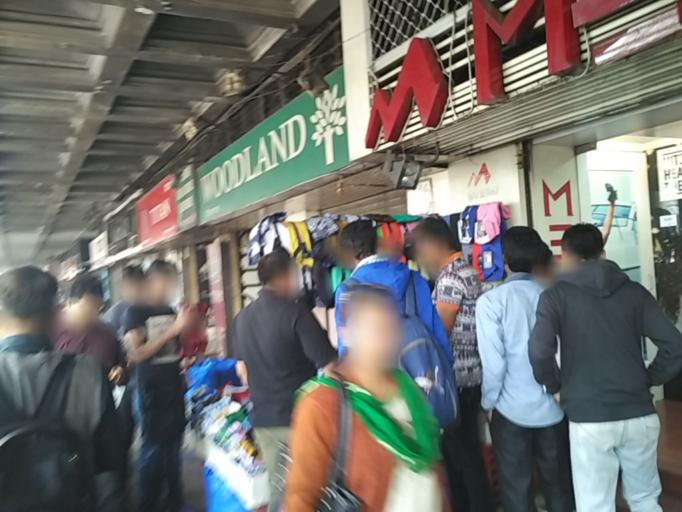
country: IN
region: West Bengal
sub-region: Kolkata
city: Bara Bazar
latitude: 22.5616
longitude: 88.3510
